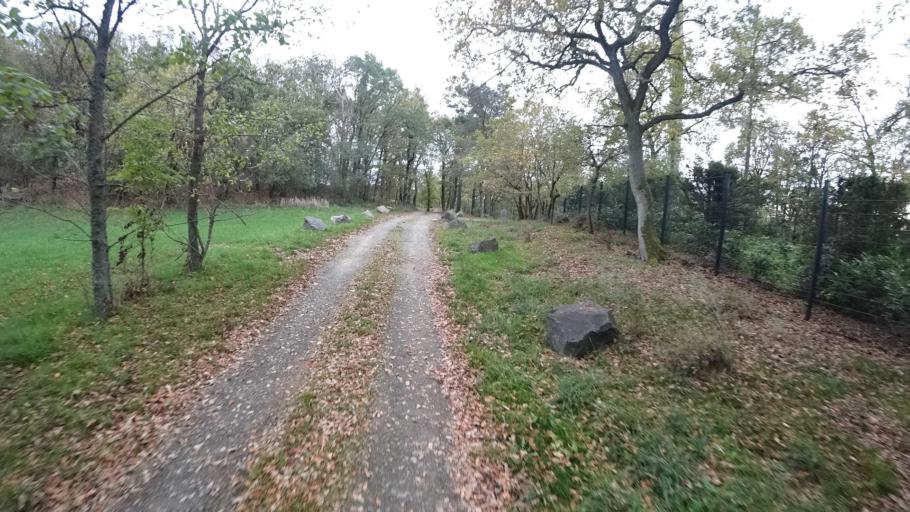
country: DE
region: Rheinland-Pfalz
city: Berg
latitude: 50.5399
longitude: 6.9348
